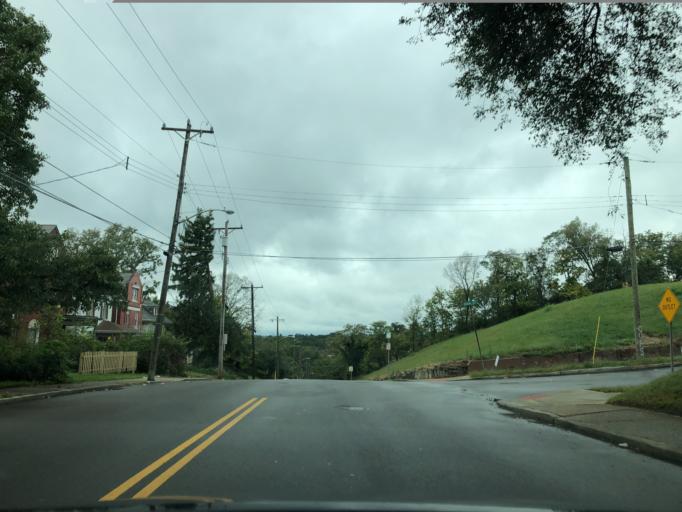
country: US
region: Ohio
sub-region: Hamilton County
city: Saint Bernard
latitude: 39.1465
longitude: -84.5033
